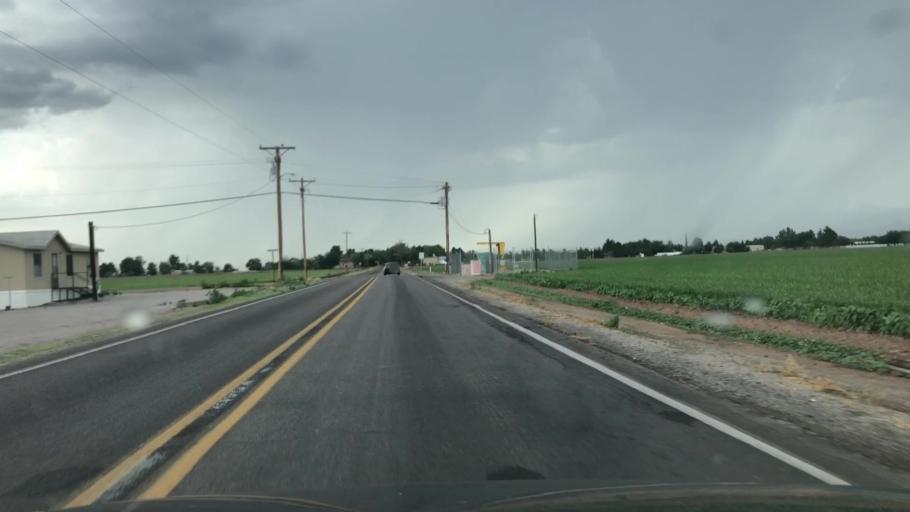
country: US
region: New Mexico
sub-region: Dona Ana County
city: Berino
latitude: 32.0445
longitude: -106.6743
